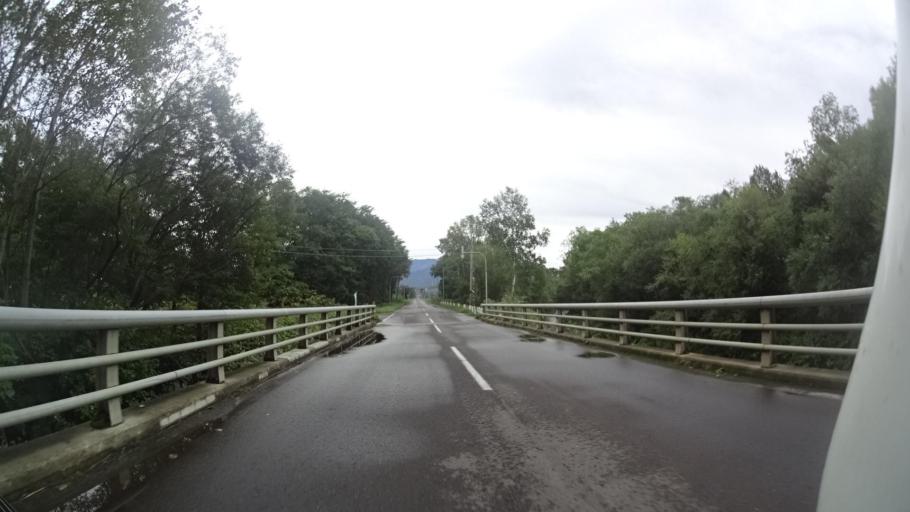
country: JP
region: Hokkaido
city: Shibetsu
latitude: 43.8733
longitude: 144.7217
